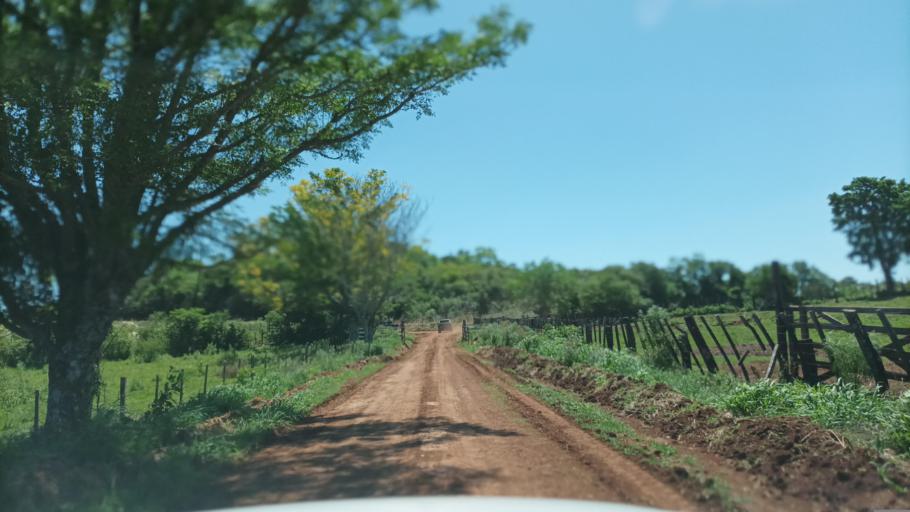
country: AR
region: Misiones
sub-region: Departamento de Apostoles
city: San Jose
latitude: -27.7875
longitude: -55.7054
